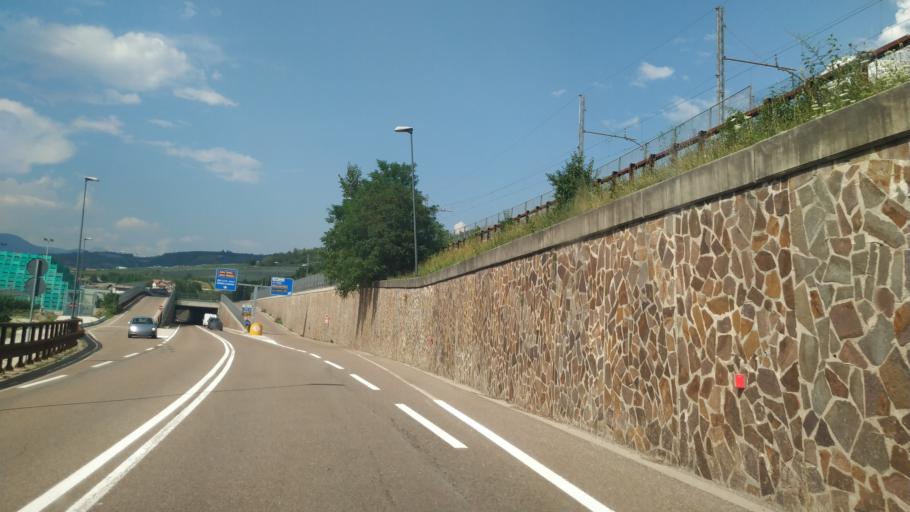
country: IT
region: Trentino-Alto Adige
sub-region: Provincia di Trento
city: Taio
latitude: 46.3089
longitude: 11.0696
